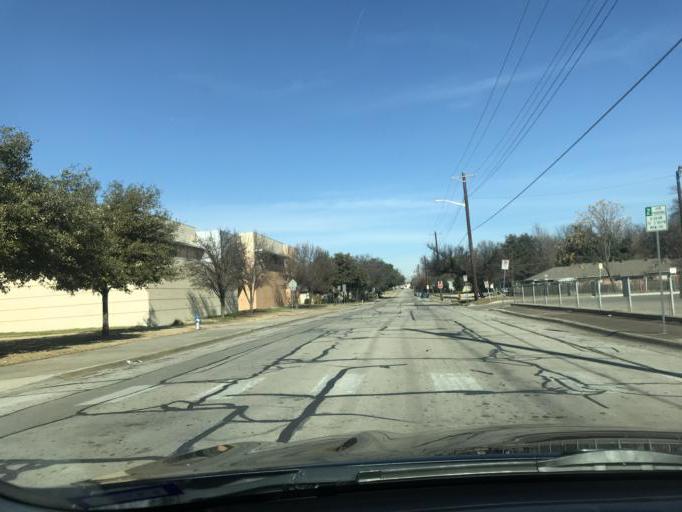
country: US
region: Texas
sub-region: Denton County
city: Denton
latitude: 33.2245
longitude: -97.1433
